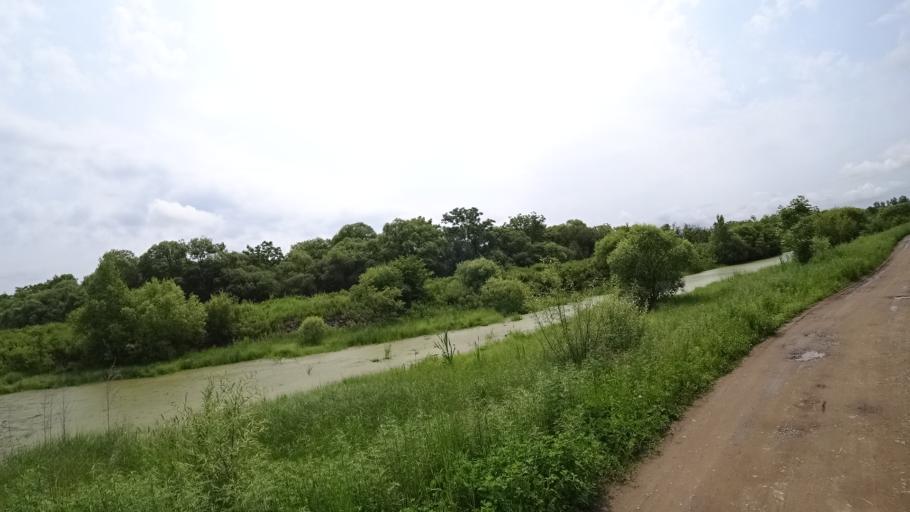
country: RU
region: Primorskiy
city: Novosysoyevka
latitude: 44.2522
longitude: 133.3741
